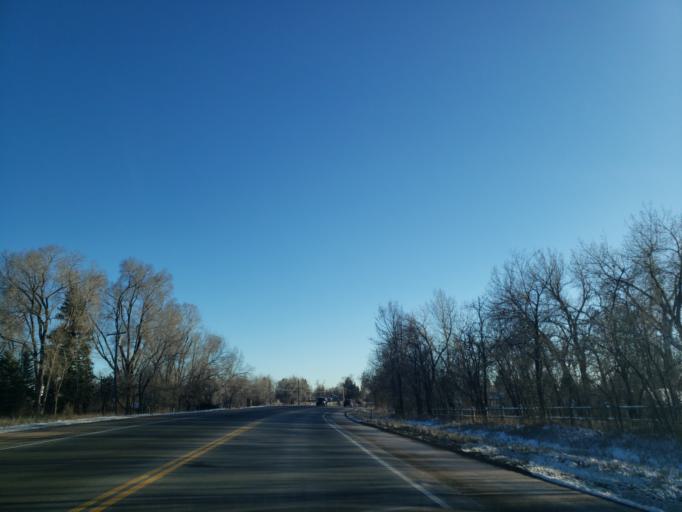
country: US
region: Colorado
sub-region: Larimer County
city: Fort Collins
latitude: 40.6320
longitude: -105.0715
